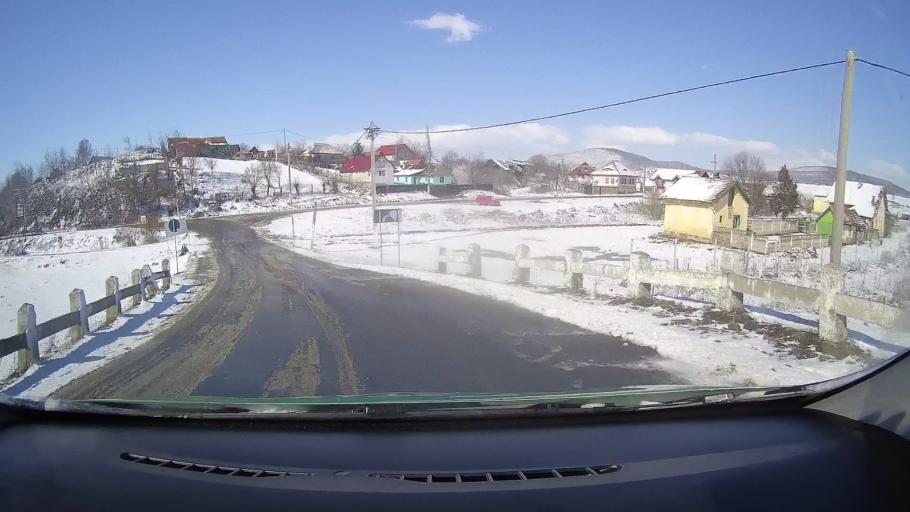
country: RO
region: Sibiu
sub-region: Comuna Rosia
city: Rosia
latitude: 45.8019
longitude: 24.3530
